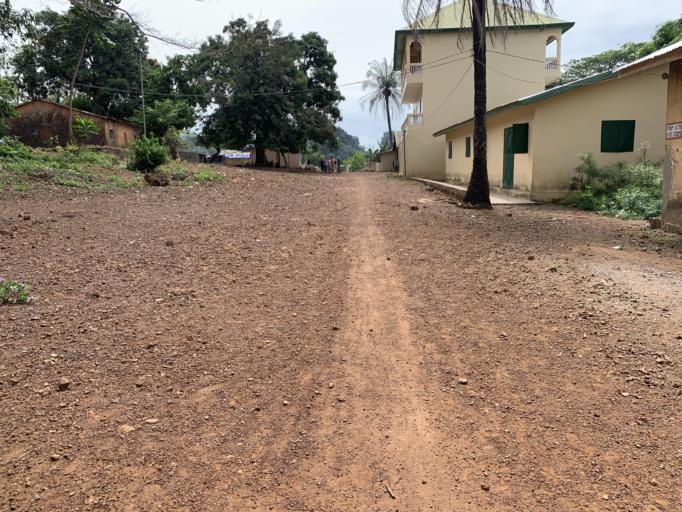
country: GN
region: Conakry
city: Camayenne
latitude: 9.5069
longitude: -13.8014
